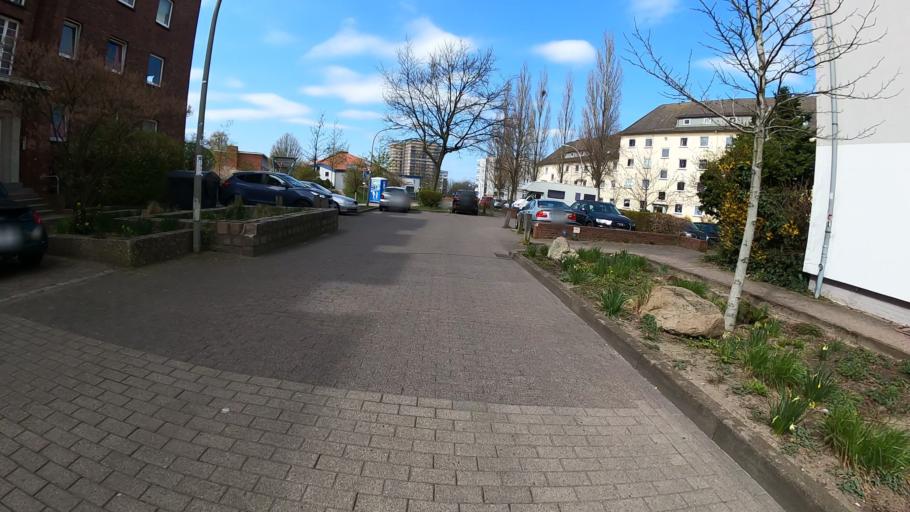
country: DE
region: Hamburg
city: Harburg
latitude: 53.4681
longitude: 9.9577
